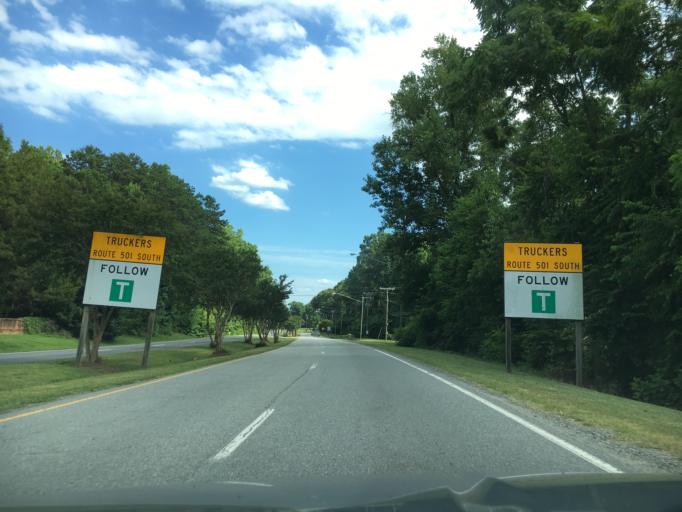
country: US
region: Virginia
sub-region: Halifax County
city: South Boston
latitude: 36.7192
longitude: -78.9176
